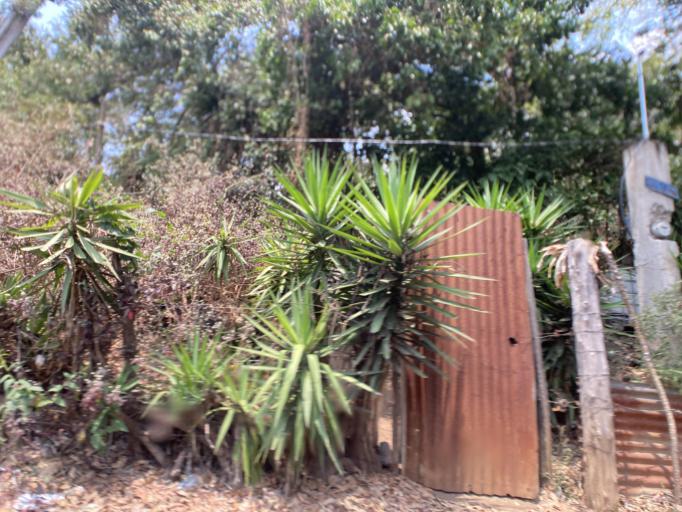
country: GT
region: Escuintla
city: San Vicente Pacaya
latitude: 14.3876
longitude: -90.5513
